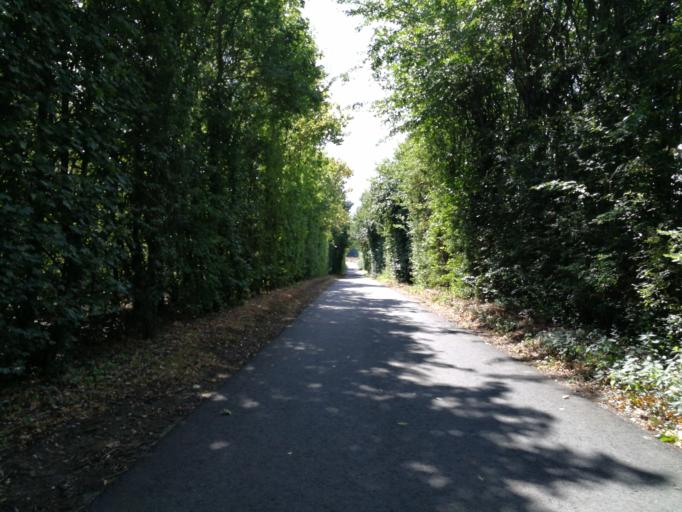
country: DE
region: North Rhine-Westphalia
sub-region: Regierungsbezirk Dusseldorf
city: Dormagen
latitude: 51.0880
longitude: 6.7834
